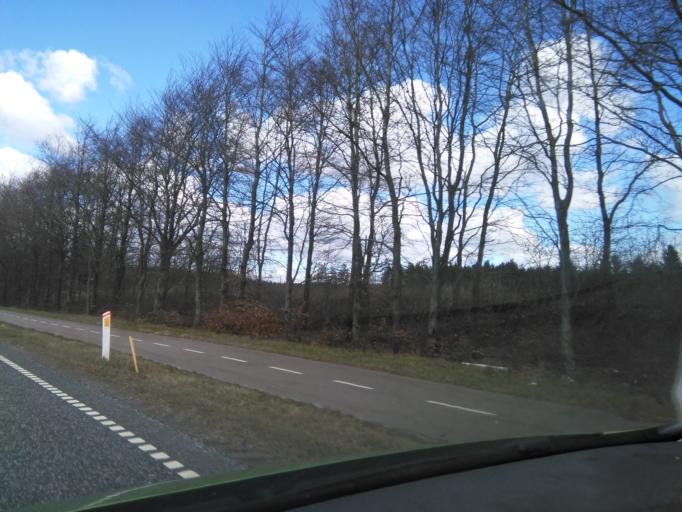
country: DK
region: Central Jutland
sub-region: Ikast-Brande Kommune
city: Bording Kirkeby
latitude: 56.1471
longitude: 9.3526
